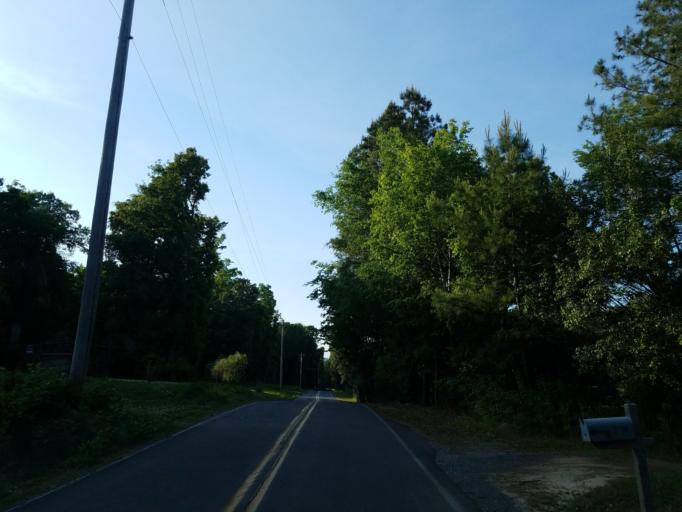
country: US
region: Georgia
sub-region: Gordon County
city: Calhoun
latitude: 34.4973
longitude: -85.1145
